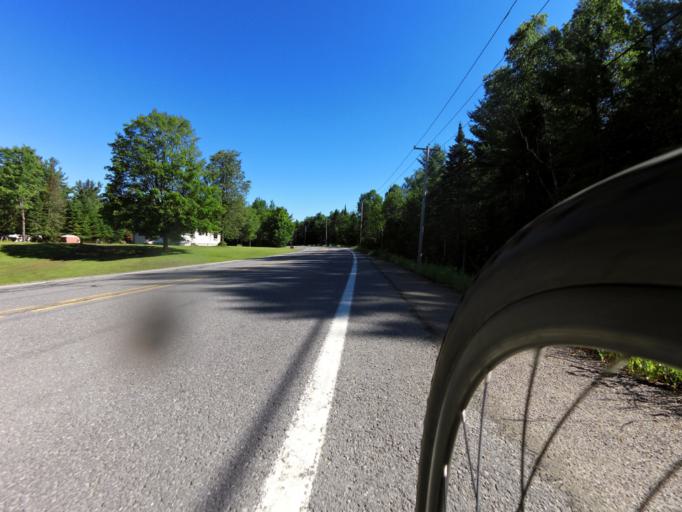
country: CA
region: Quebec
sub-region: Laurentides
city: Brownsburg-Chatham
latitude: 45.8665
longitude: -74.5637
